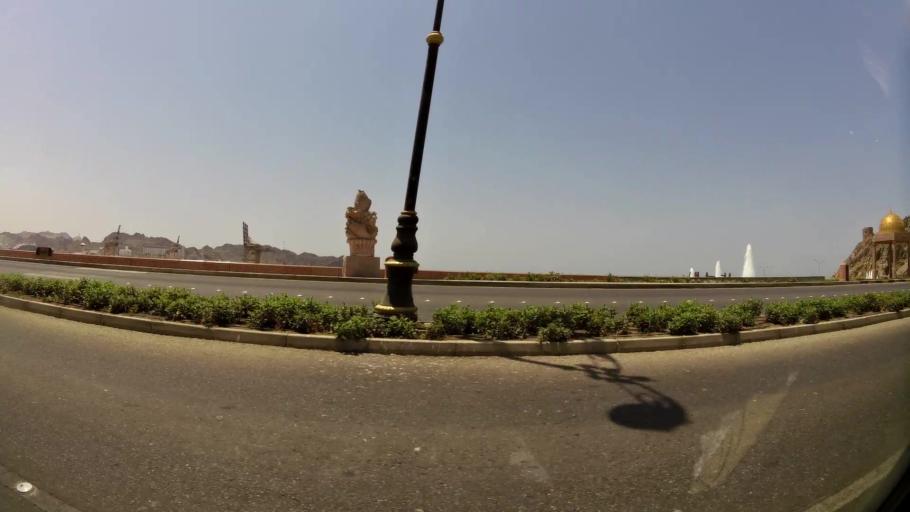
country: OM
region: Muhafazat Masqat
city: Muscat
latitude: 23.6243
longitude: 58.5783
